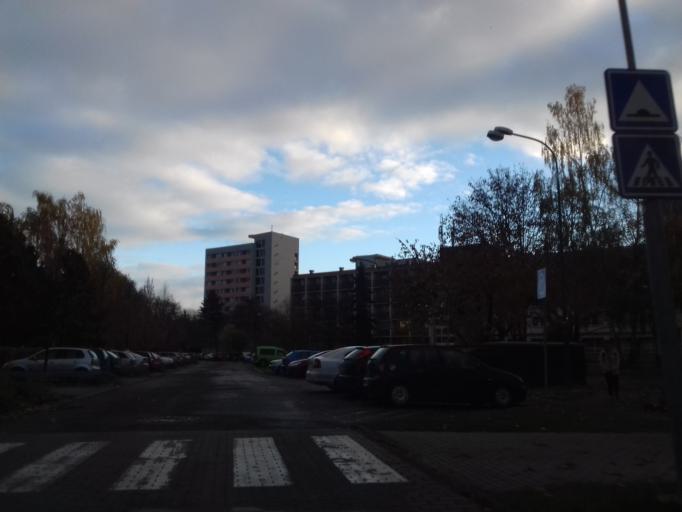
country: CZ
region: Olomoucky
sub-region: Okres Olomouc
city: Olomouc
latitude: 49.5920
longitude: 17.2644
